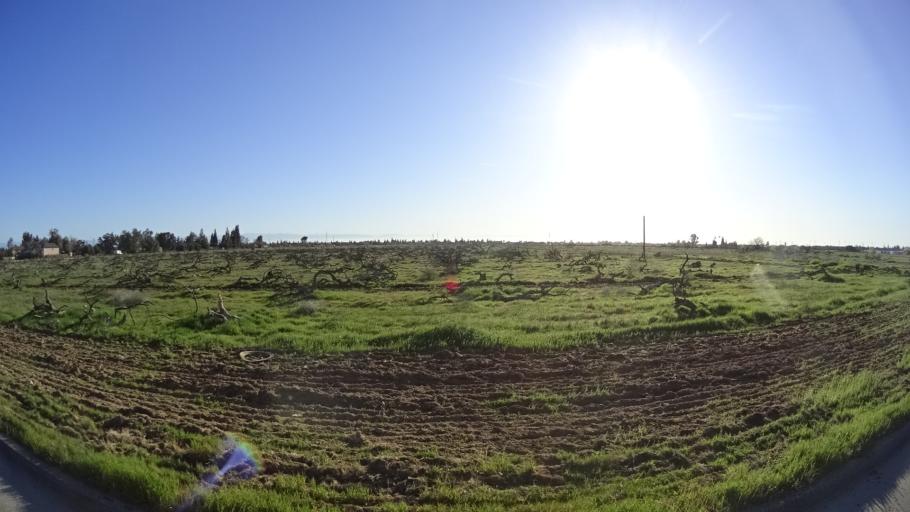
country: US
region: California
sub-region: Fresno County
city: Biola
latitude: 36.8131
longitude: -119.9165
